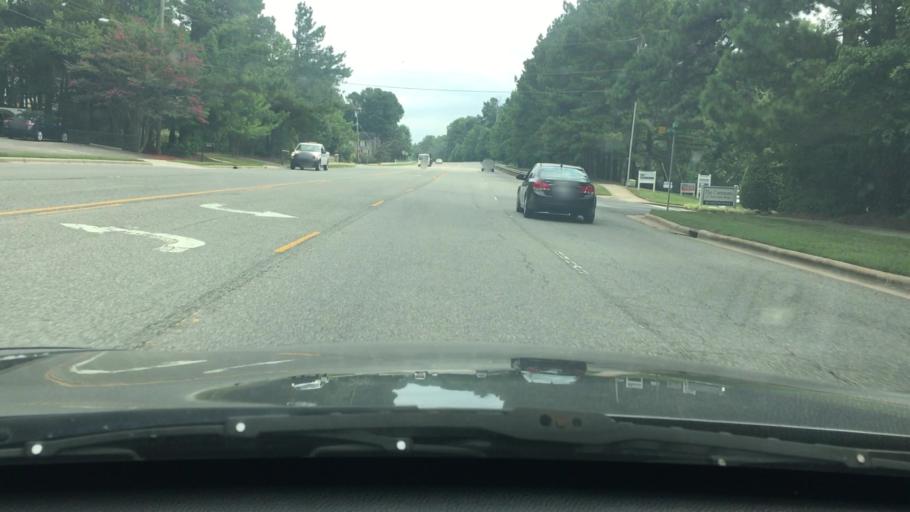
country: US
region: North Carolina
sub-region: Wake County
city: West Raleigh
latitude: 35.8540
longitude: -78.7114
